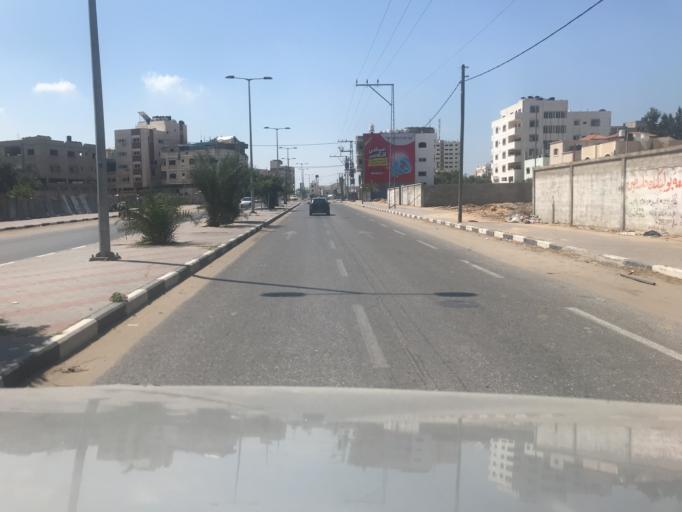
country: PS
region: Gaza Strip
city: Jabalya
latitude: 31.5459
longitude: 34.4732
